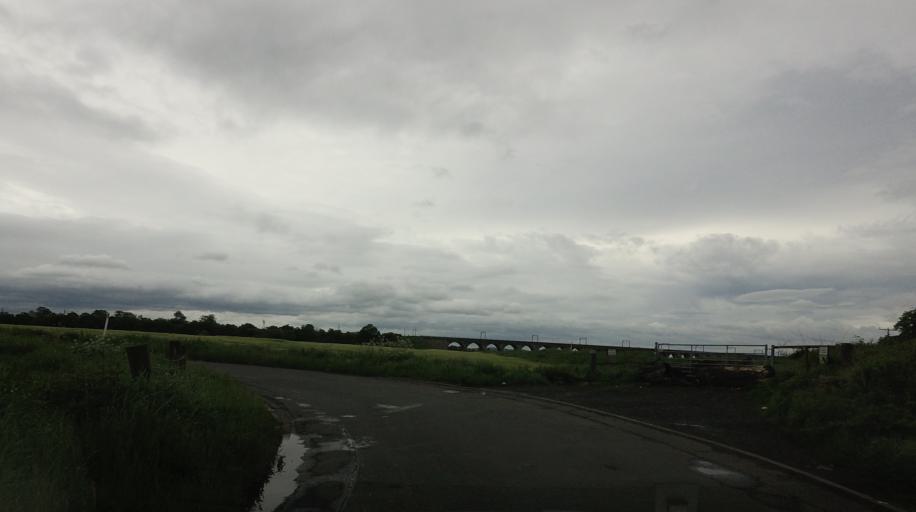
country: GB
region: Scotland
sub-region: Edinburgh
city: Newbridge
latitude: 55.9324
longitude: -3.4315
